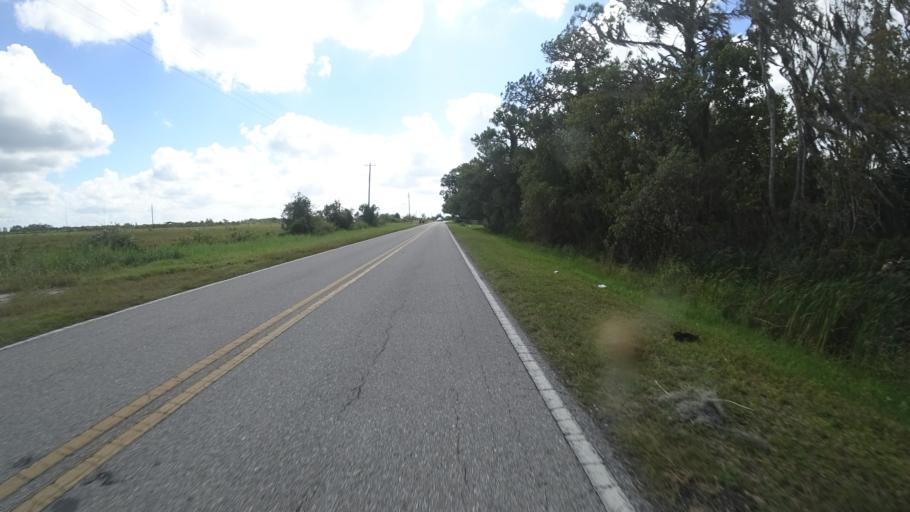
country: US
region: Florida
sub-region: Sarasota County
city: Lake Sarasota
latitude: 27.4035
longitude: -82.1316
